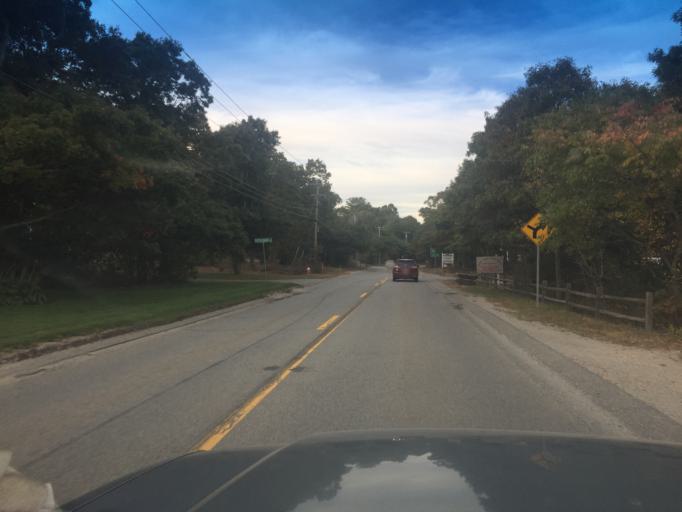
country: US
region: Massachusetts
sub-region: Barnstable County
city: Pocasset
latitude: 41.6831
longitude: -70.5947
